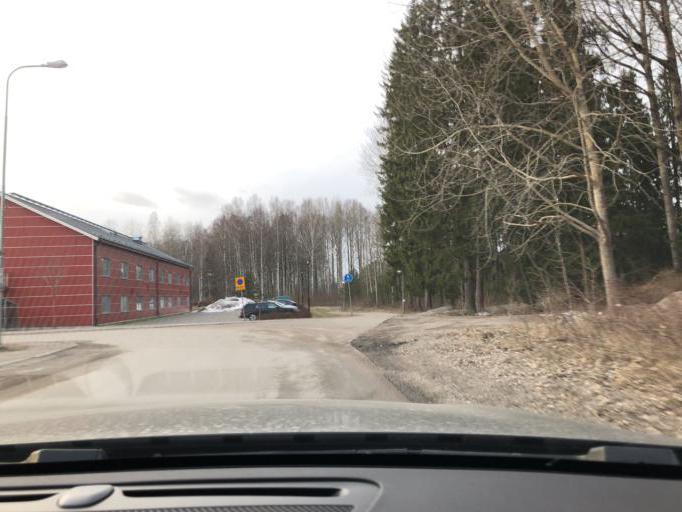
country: SE
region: Uppsala
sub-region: Tierps Kommun
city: Tierp
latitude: 60.3489
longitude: 17.5011
